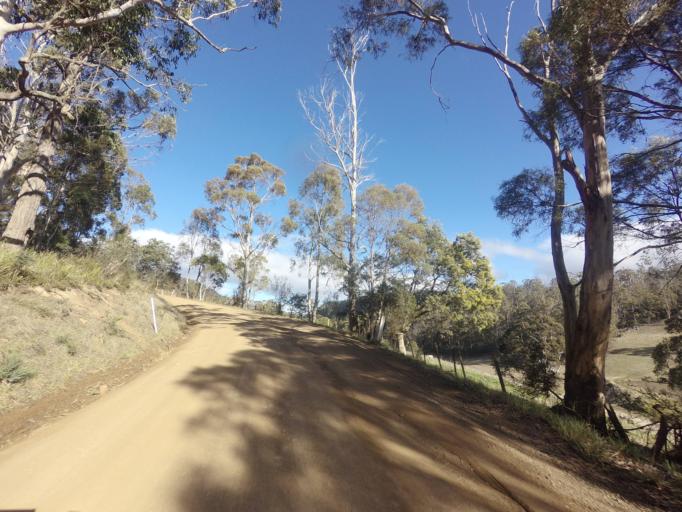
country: AU
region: Tasmania
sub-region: Derwent Valley
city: New Norfolk
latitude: -42.7085
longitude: 147.0220
